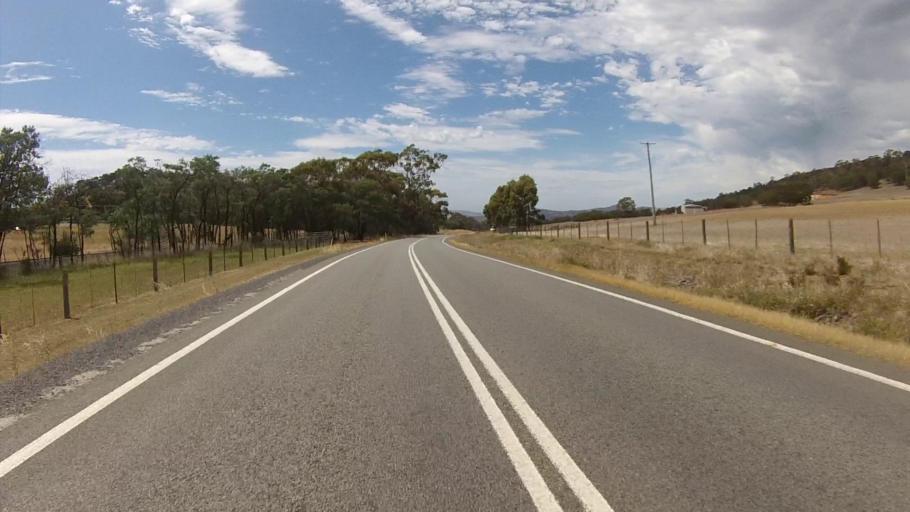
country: AU
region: Tasmania
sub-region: Brighton
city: Old Beach
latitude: -42.6698
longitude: 147.3870
